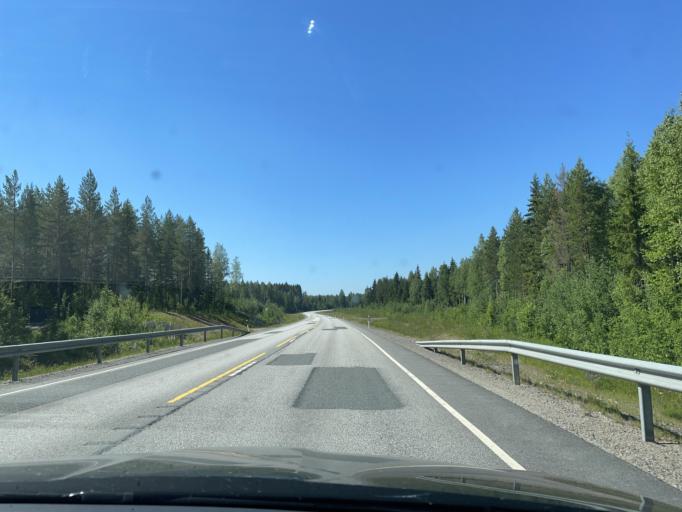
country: FI
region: Central Finland
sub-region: Saarijaervi-Viitasaari
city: Viitasaari
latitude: 63.1698
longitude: 26.0011
